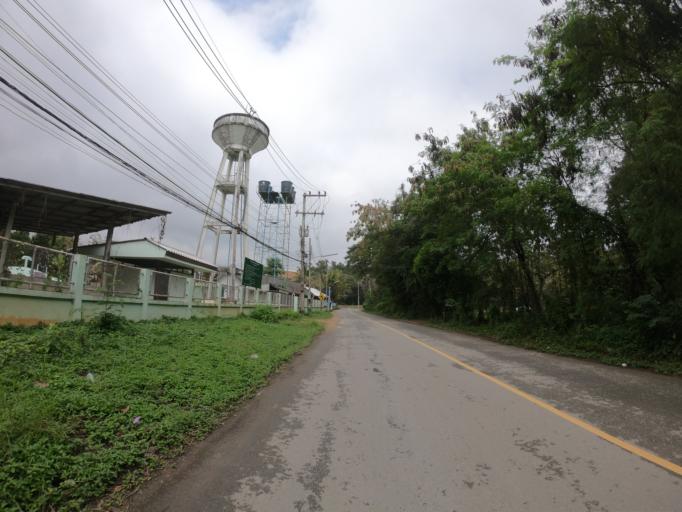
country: TH
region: Chiang Mai
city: San Sai
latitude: 18.8437
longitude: 99.0052
